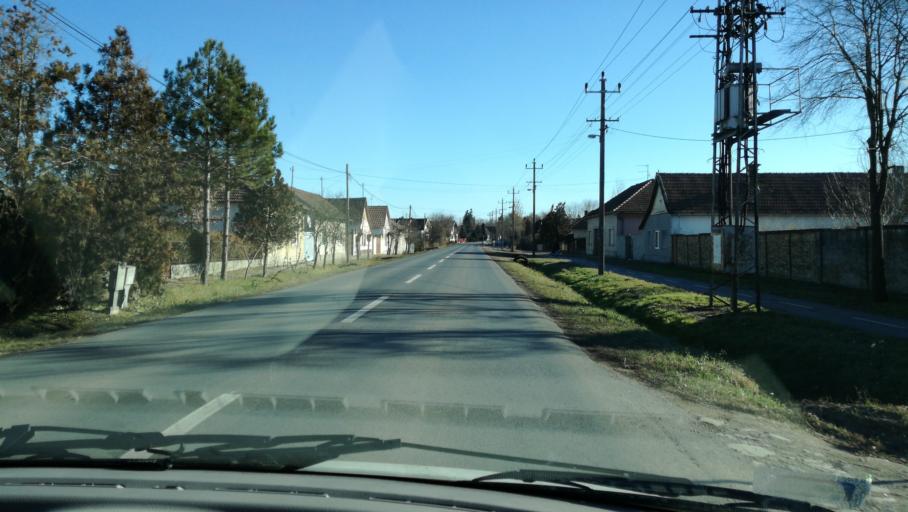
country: HU
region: Csongrad
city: Roszke
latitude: 46.1487
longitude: 19.9756
